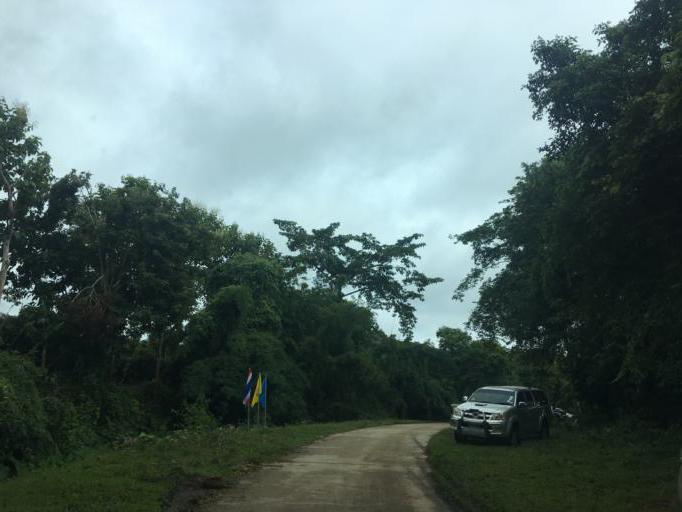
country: TH
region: Chiang Rai
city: Mae Lao
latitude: 19.6933
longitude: 99.6564
